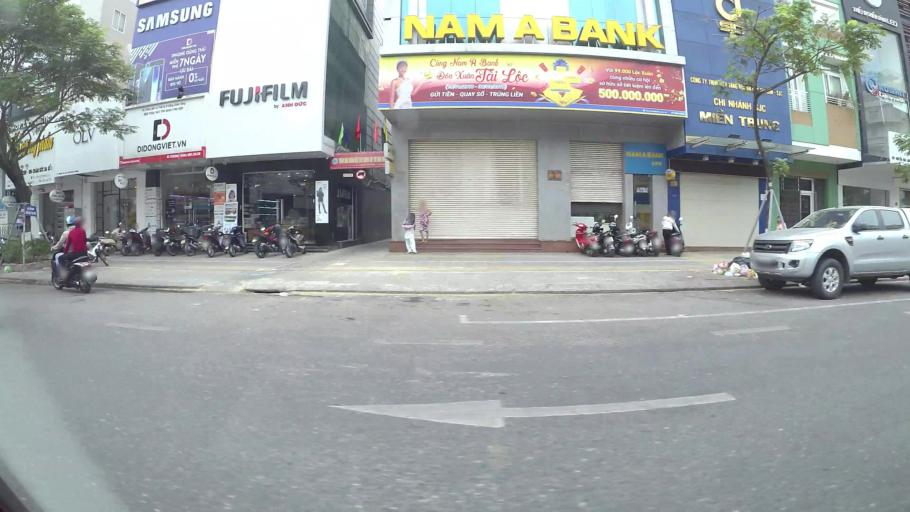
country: VN
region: Da Nang
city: Da Nang
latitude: 16.0599
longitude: 108.2143
